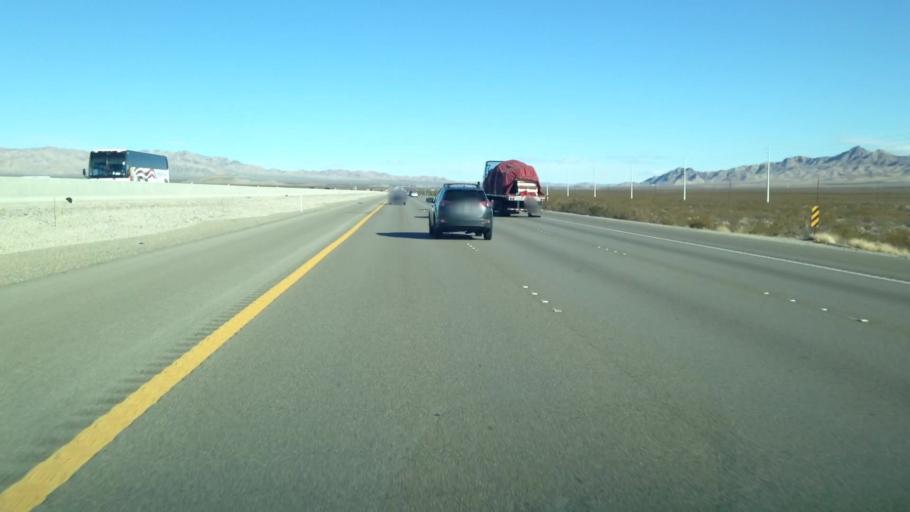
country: US
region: Nevada
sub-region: Clark County
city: Sandy Valley
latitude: 35.6881
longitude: -115.3746
